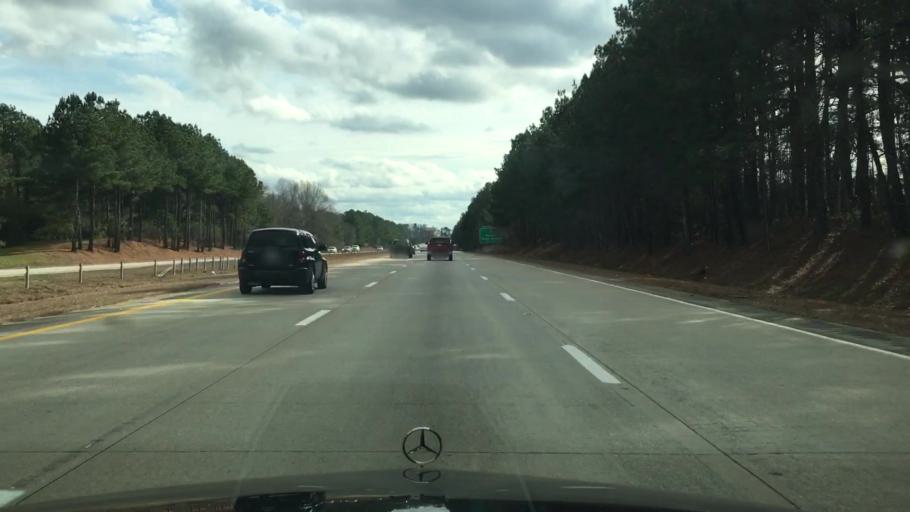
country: US
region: North Carolina
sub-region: Johnston County
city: Benson
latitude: 35.4192
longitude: -78.5285
